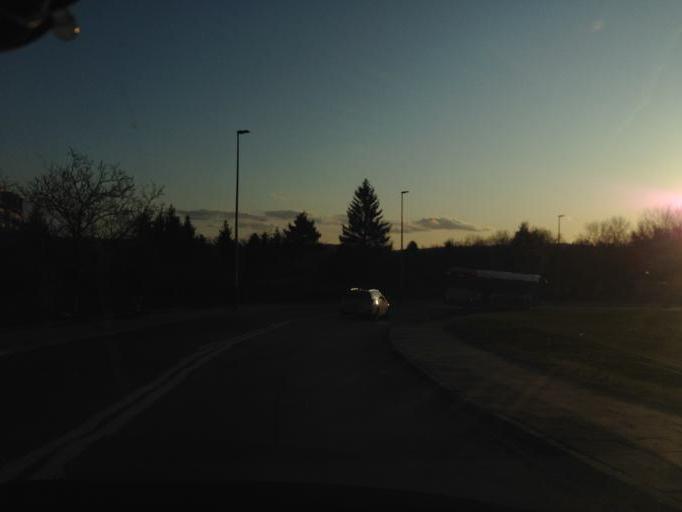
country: PL
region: Lesser Poland Voivodeship
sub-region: Krakow
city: Krakow
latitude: 50.0806
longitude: 19.8917
